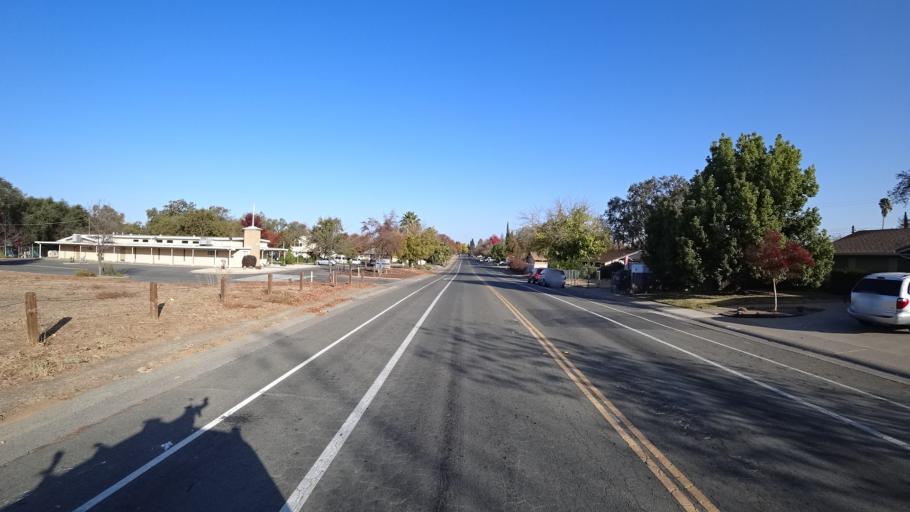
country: US
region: California
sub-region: Sacramento County
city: Citrus Heights
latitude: 38.6971
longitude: -121.2694
